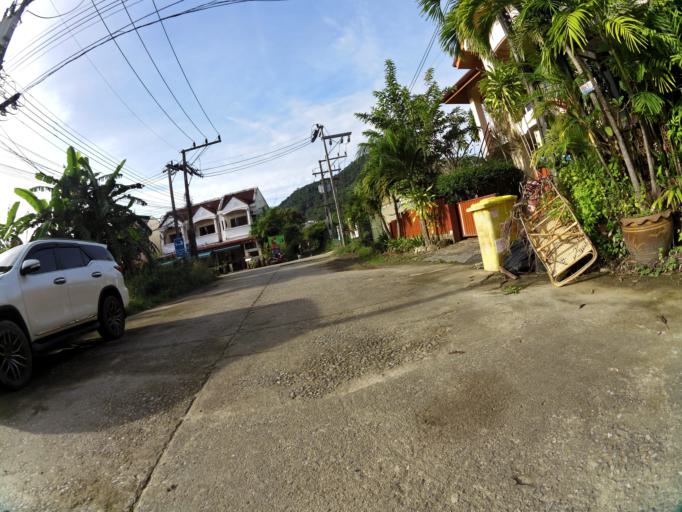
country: TH
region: Phuket
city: Patong
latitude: 7.9495
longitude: 98.2814
